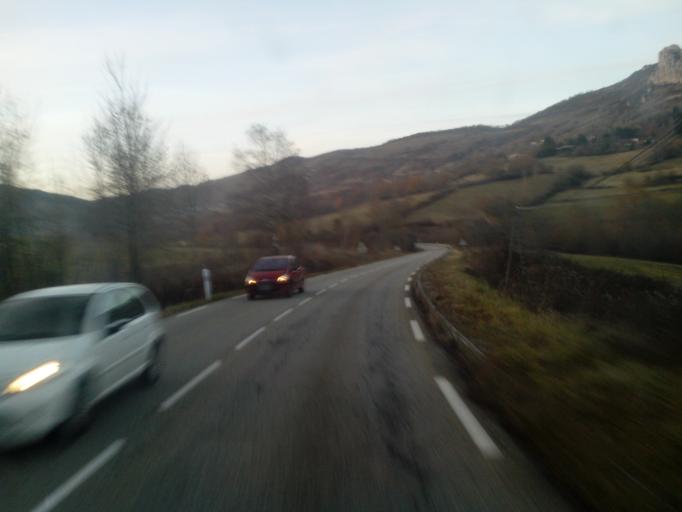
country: FR
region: Midi-Pyrenees
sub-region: Departement de l'Ariege
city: Lavelanet
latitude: 42.9210
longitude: 1.7520
